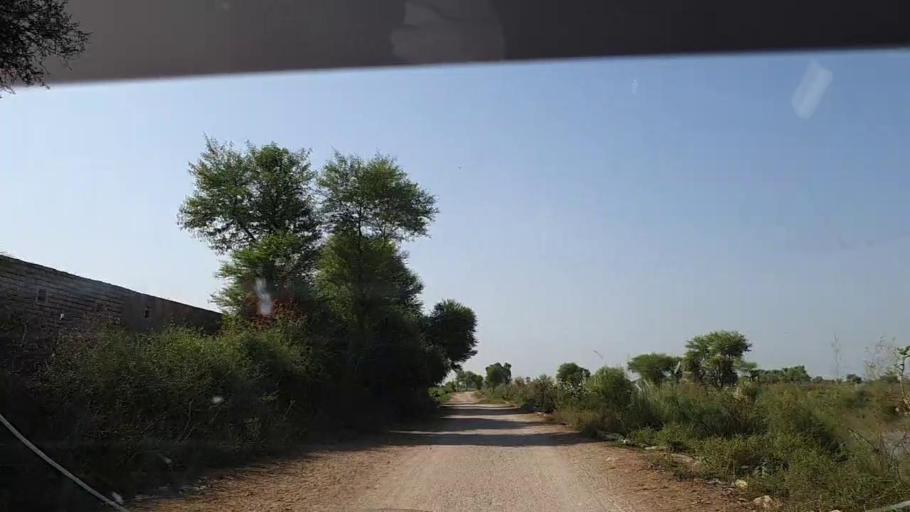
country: PK
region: Sindh
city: Ghauspur
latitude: 28.2023
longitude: 69.0392
